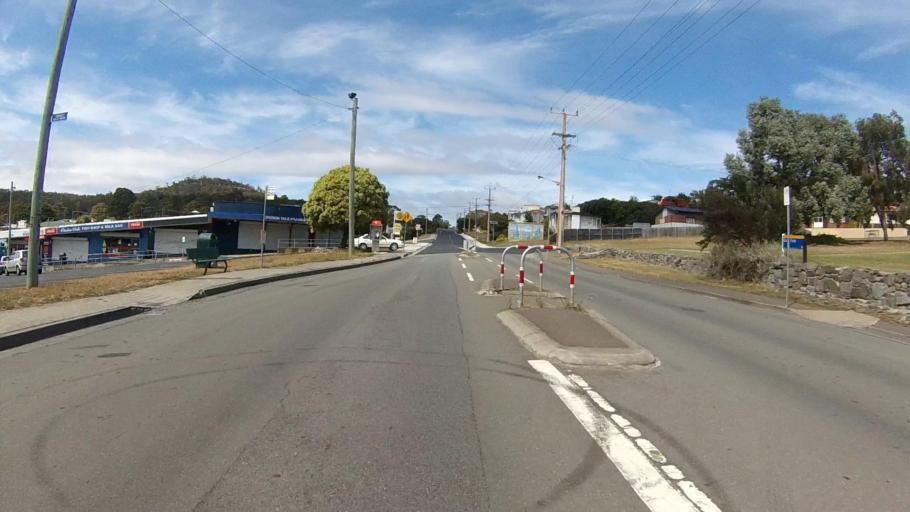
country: AU
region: Tasmania
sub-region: Clarence
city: Lindisfarne
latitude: -42.8124
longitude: 147.3513
